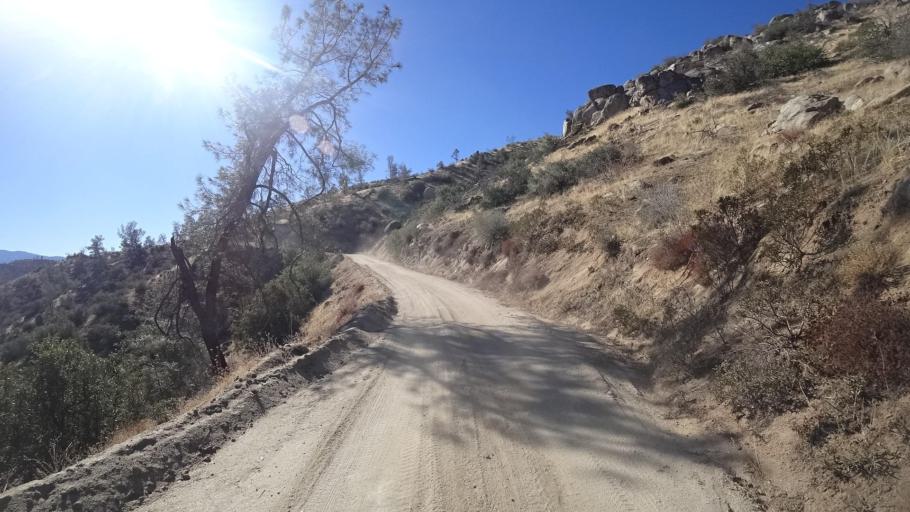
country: US
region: California
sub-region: Kern County
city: Wofford Heights
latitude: 35.7051
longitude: -118.4888
